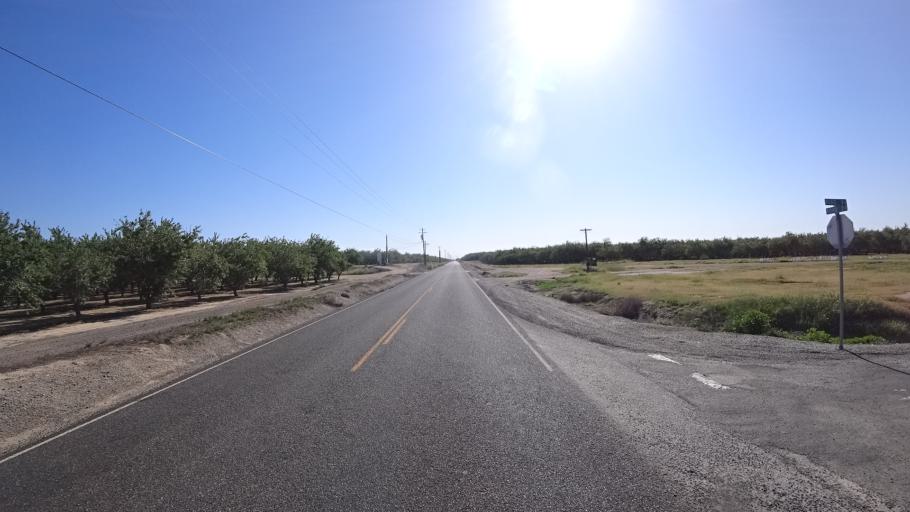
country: US
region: California
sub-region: Glenn County
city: Hamilton City
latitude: 39.7091
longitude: -122.0548
